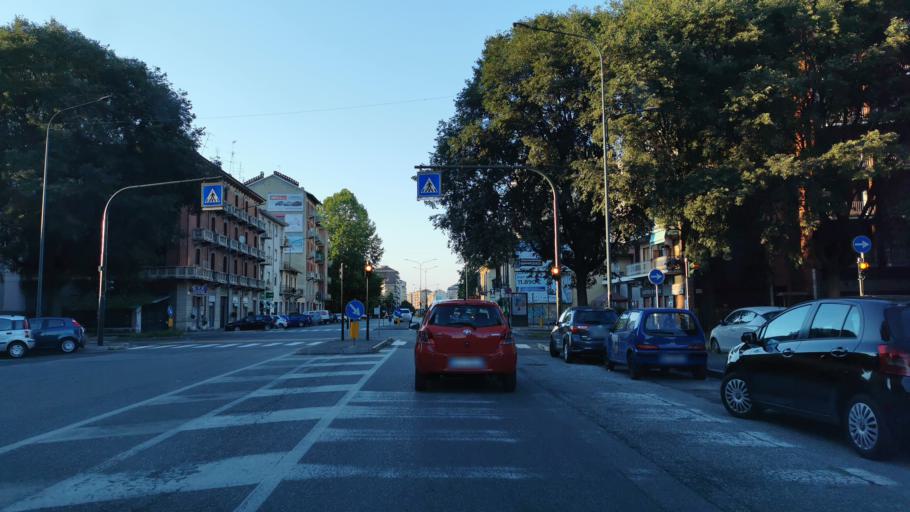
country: IT
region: Piedmont
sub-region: Provincia di Torino
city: Turin
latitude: 45.1007
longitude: 7.6940
